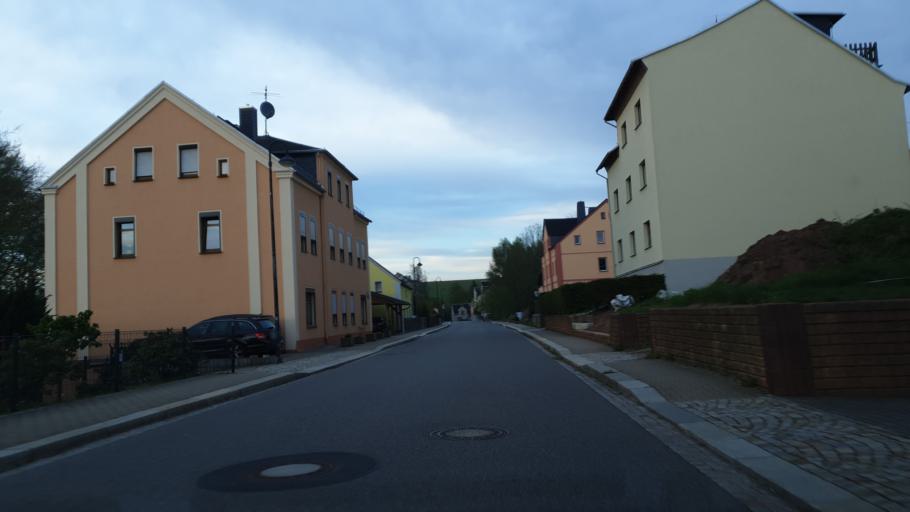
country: DE
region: Saxony
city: Gersdorf
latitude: 50.7438
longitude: 12.7207
